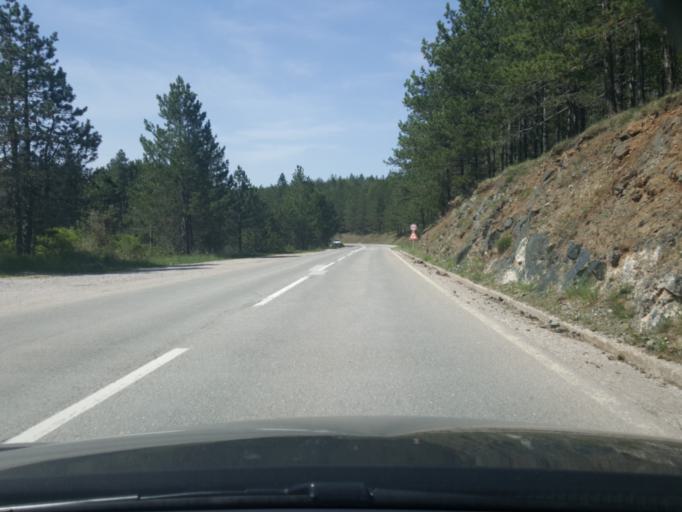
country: RS
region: Central Serbia
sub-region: Zlatiborski Okrug
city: Cajetina
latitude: 43.8306
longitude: 19.6396
